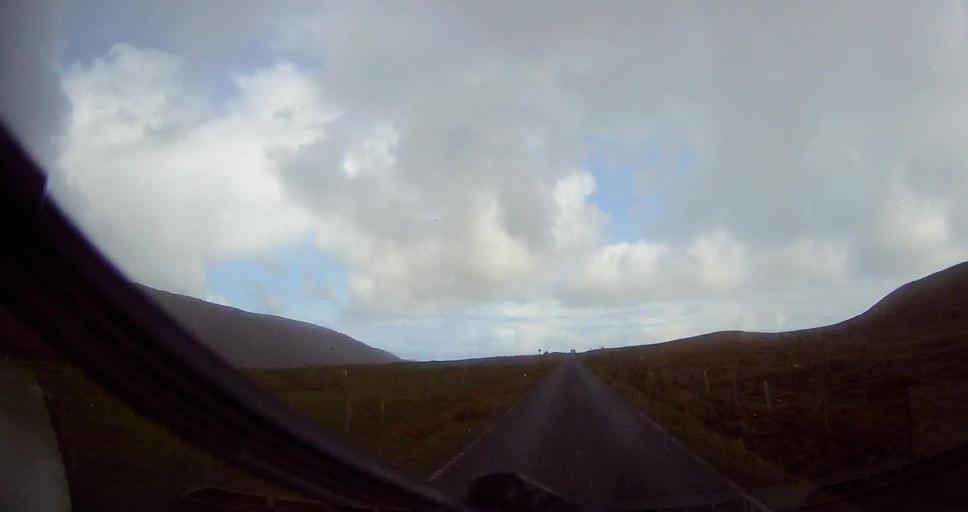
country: GB
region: Scotland
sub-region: Shetland Islands
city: Lerwick
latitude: 60.5549
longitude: -1.3399
